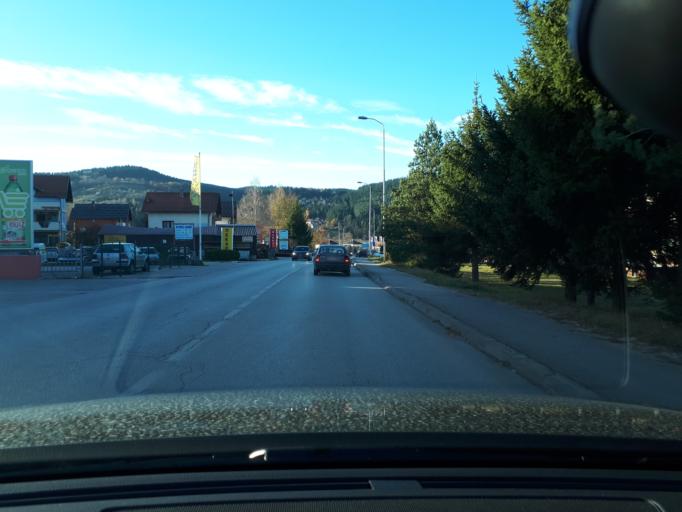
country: BA
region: Republika Srpska
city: Pale
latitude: 43.8141
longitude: 18.5636
